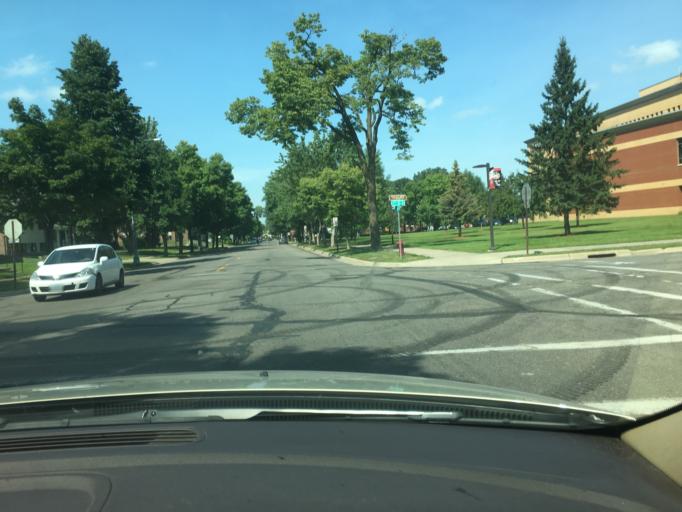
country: US
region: Minnesota
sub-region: Stearns County
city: Saint Cloud
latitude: 45.5526
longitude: -94.1546
